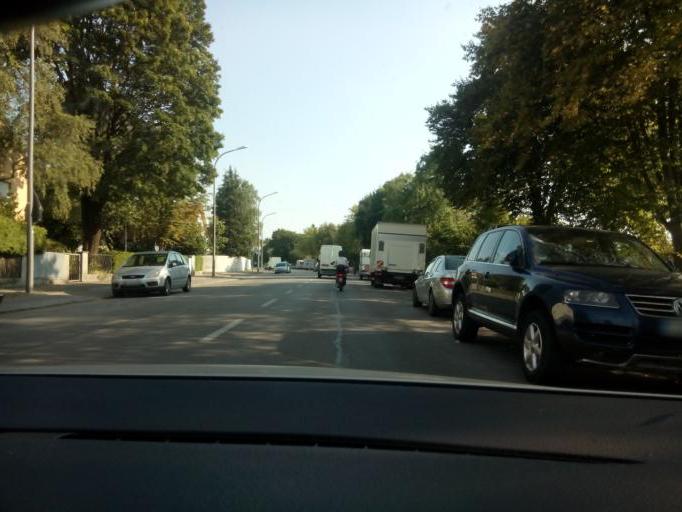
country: DE
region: Bavaria
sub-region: Upper Bavaria
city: Unterhaching
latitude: 48.1002
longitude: 11.6067
